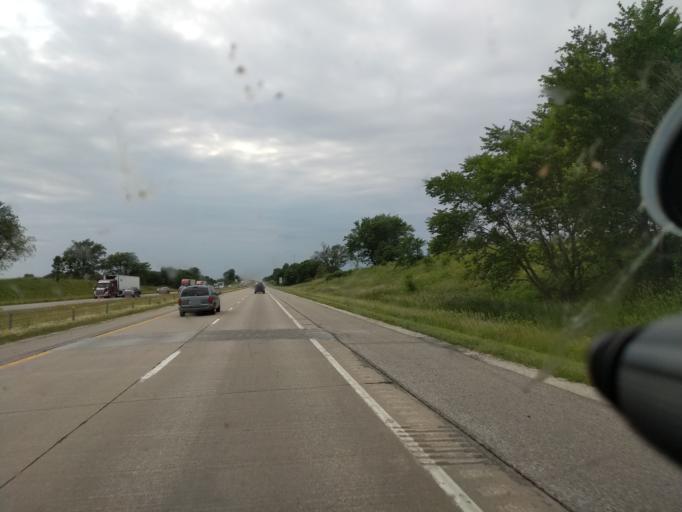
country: US
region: Iowa
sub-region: Dallas County
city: Waukee
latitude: 41.5611
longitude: -93.8902
